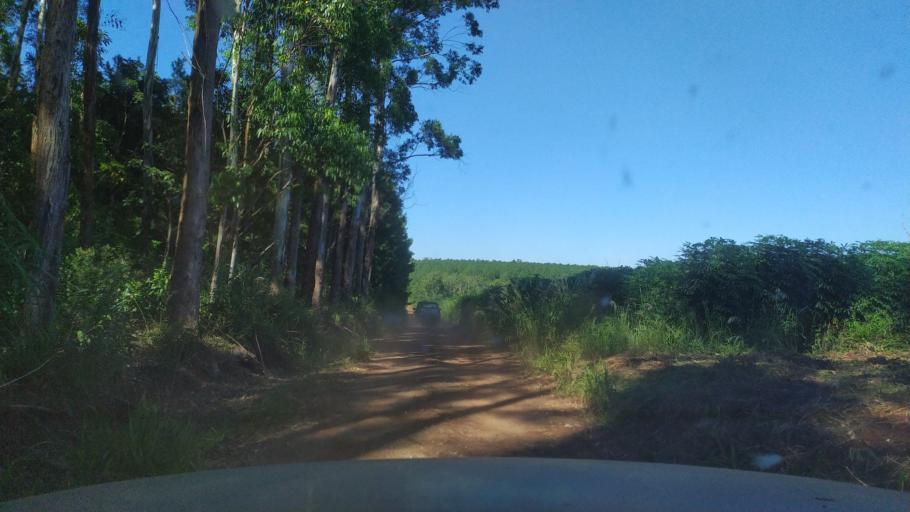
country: AR
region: Misiones
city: Caraguatay
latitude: -26.6727
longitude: -54.6970
